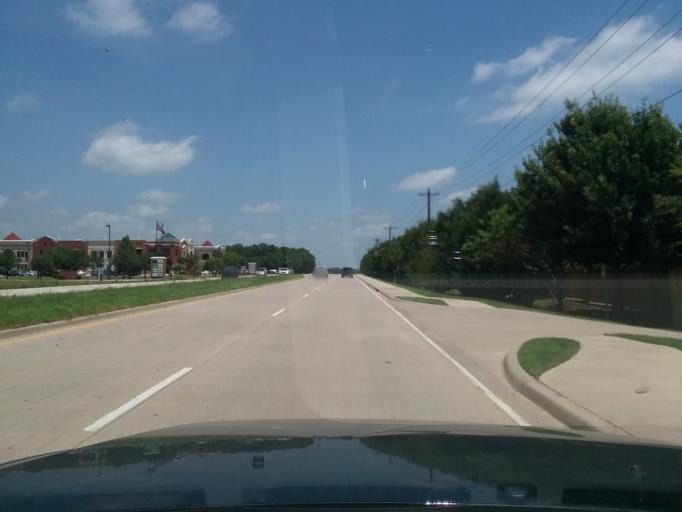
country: US
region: Texas
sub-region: Denton County
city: Bartonville
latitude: 33.0912
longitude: -97.1312
